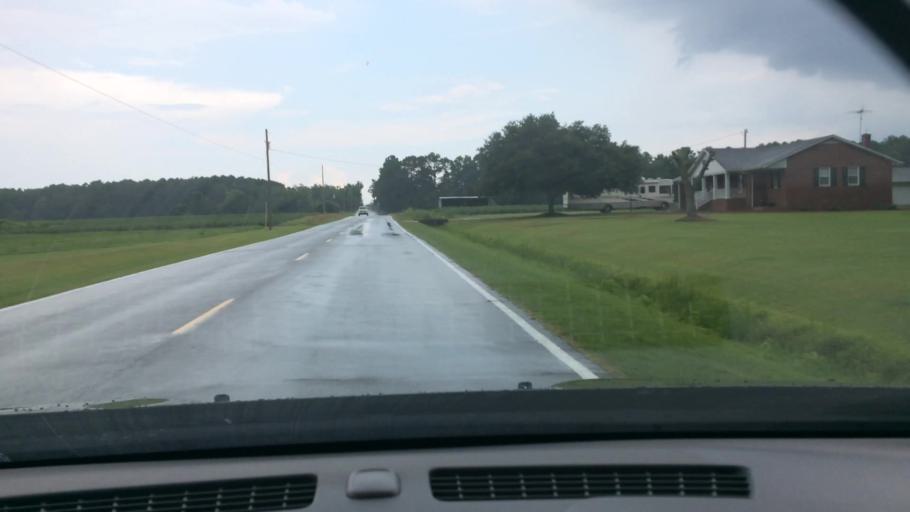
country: US
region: North Carolina
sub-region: Pitt County
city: Winterville
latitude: 35.5012
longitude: -77.3800
